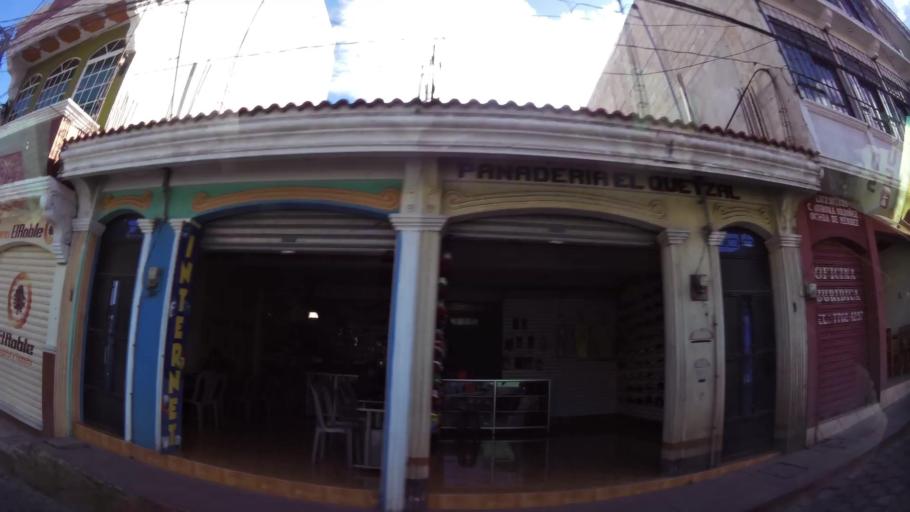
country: GT
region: Solola
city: Solola
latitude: 14.7708
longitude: -91.1820
